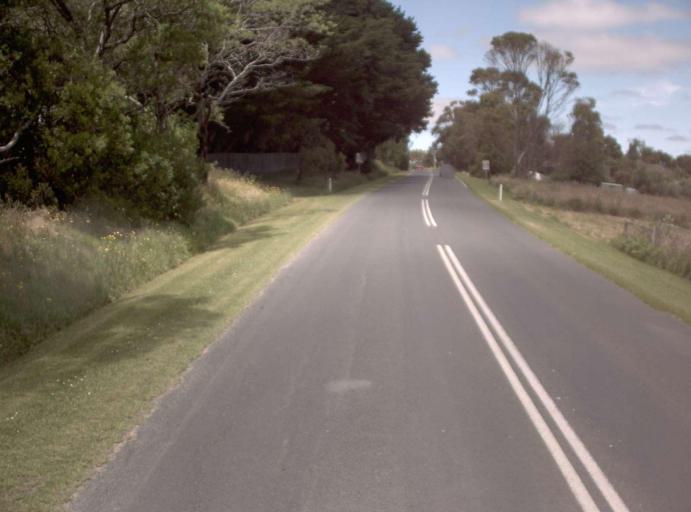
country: AU
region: Victoria
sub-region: Bass Coast
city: North Wonthaggi
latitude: -38.7001
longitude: 146.0879
